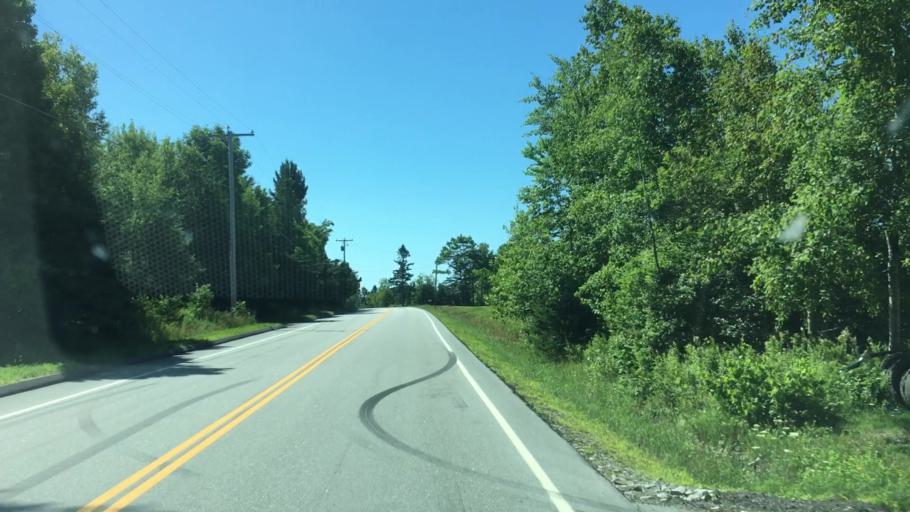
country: US
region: Maine
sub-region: Hancock County
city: Orland
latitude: 44.5339
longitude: -68.6773
